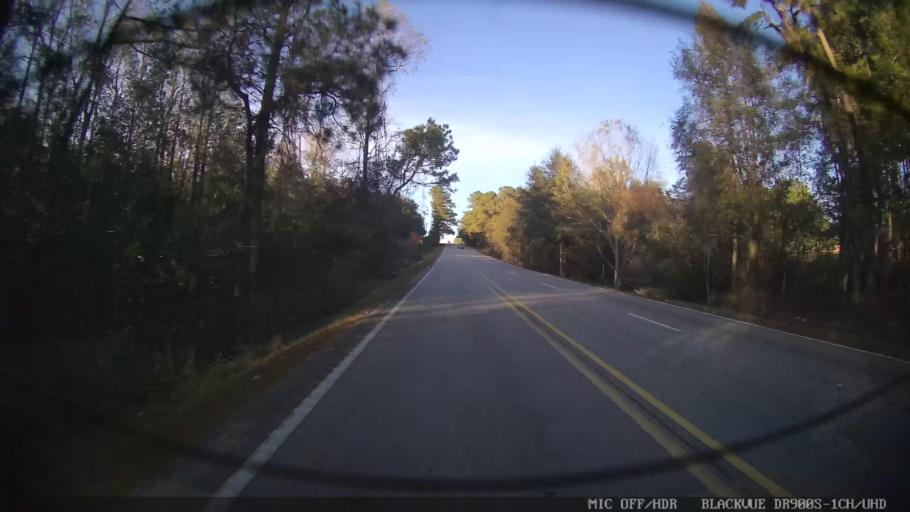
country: US
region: Mississippi
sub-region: Lamar County
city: Purvis
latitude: 31.0943
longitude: -89.4147
